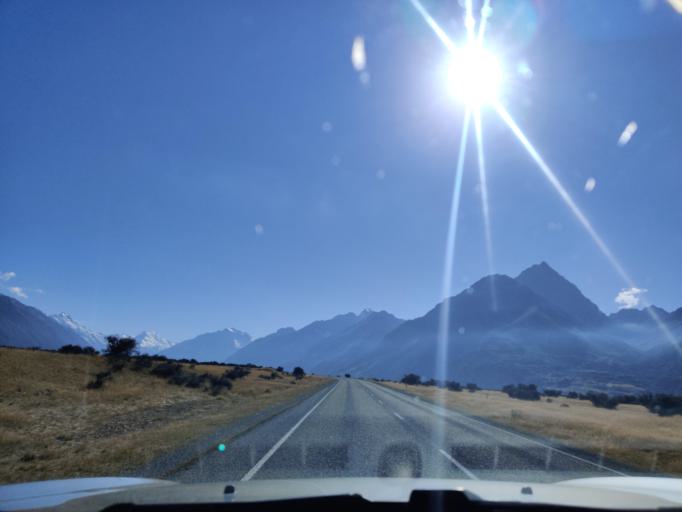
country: NZ
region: Canterbury
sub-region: Timaru District
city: Pleasant Point
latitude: -43.7847
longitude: 170.1216
